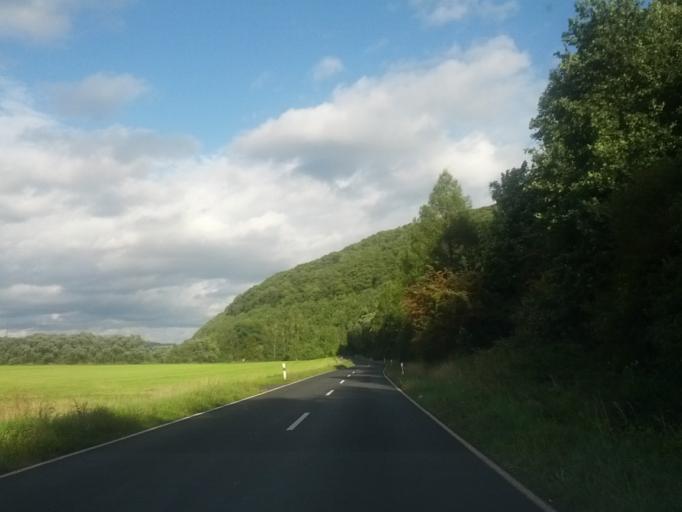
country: DE
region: Thuringia
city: Lauchroden
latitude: 50.9955
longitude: 10.1713
